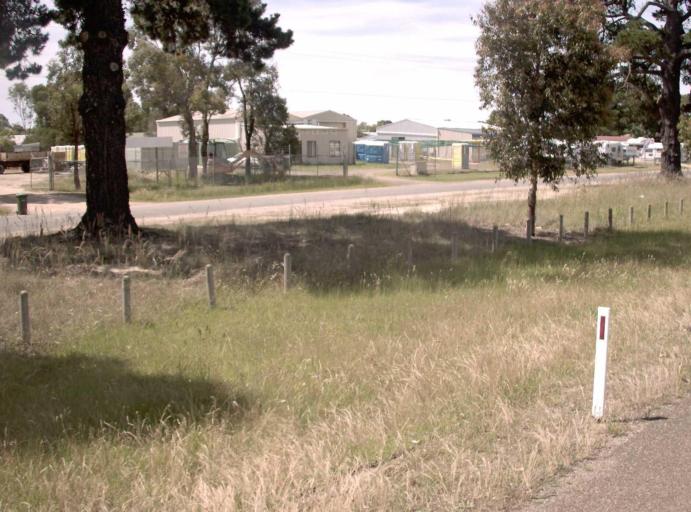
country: AU
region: Victoria
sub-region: Wellington
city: Sale
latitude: -37.9633
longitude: 147.0875
